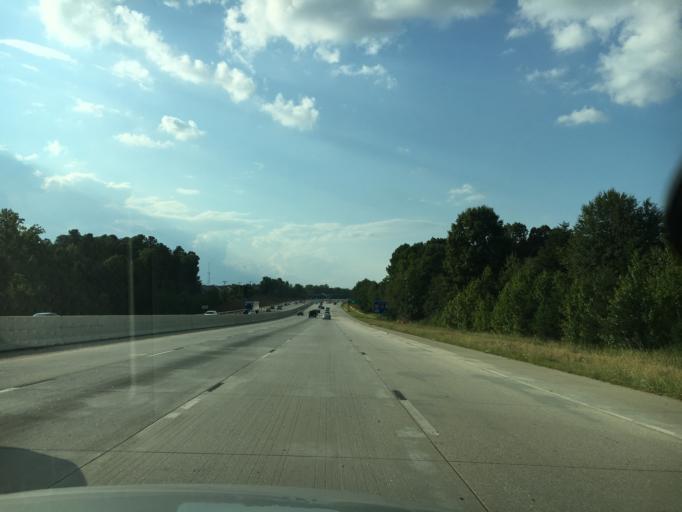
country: US
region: South Carolina
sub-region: Greenville County
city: Mauldin
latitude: 34.8091
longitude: -82.2852
